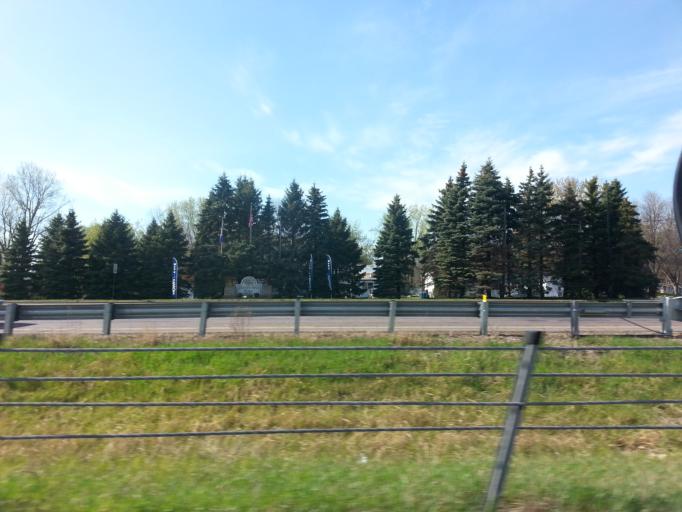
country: US
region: Minnesota
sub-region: Ramsey County
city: North Saint Paul
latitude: 45.0252
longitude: -92.9753
